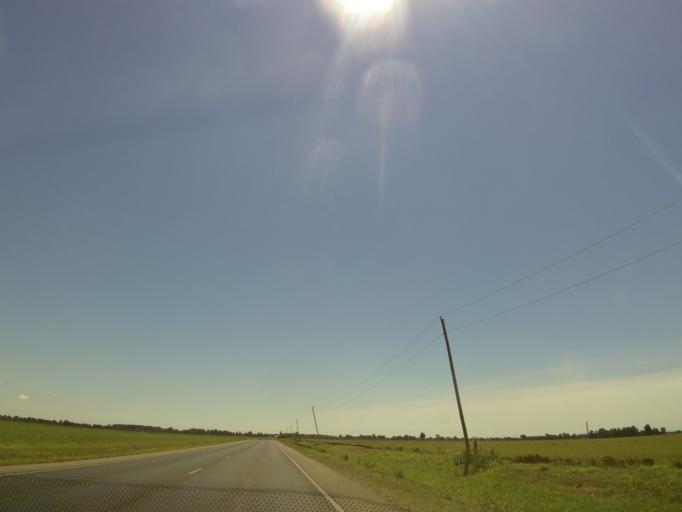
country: US
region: Missouri
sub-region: New Madrid County
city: Lilbourn
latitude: 36.5555
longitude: -89.6363
